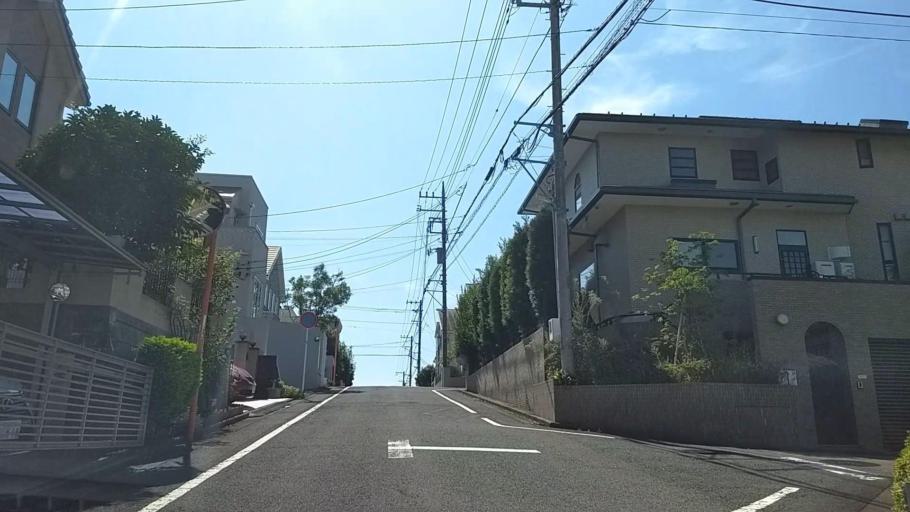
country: JP
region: Tokyo
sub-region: Machida-shi
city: Machida
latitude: 35.5629
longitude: 139.5414
